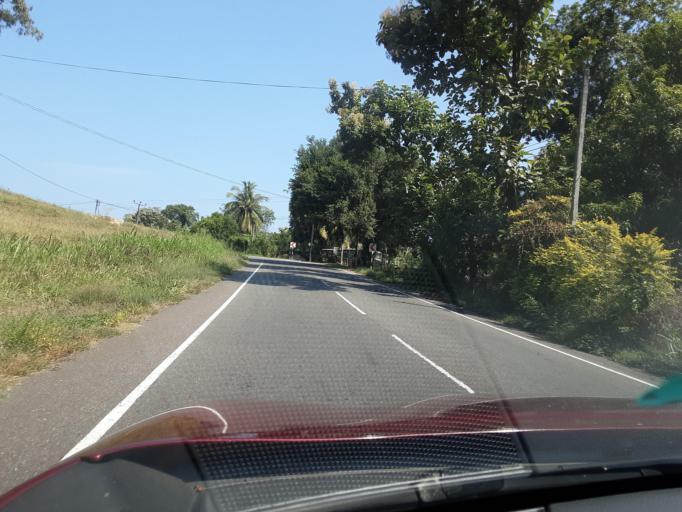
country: LK
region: Uva
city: Badulla
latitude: 7.1555
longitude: 81.0552
